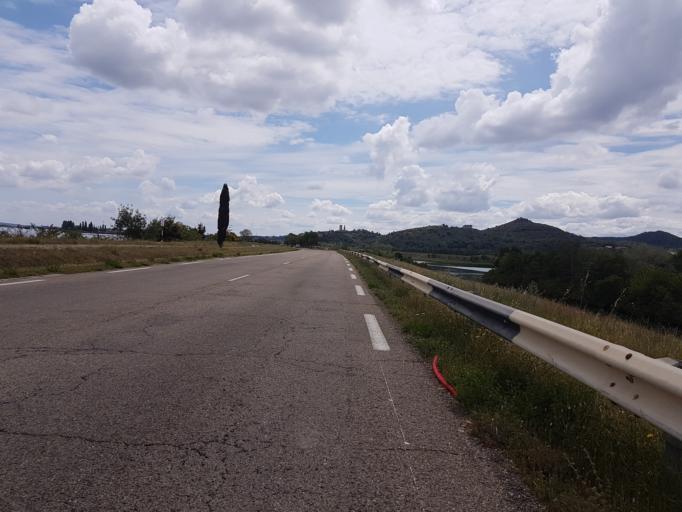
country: FR
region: Languedoc-Roussillon
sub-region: Departement du Gard
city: Vallabregues
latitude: 43.8546
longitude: 4.6177
